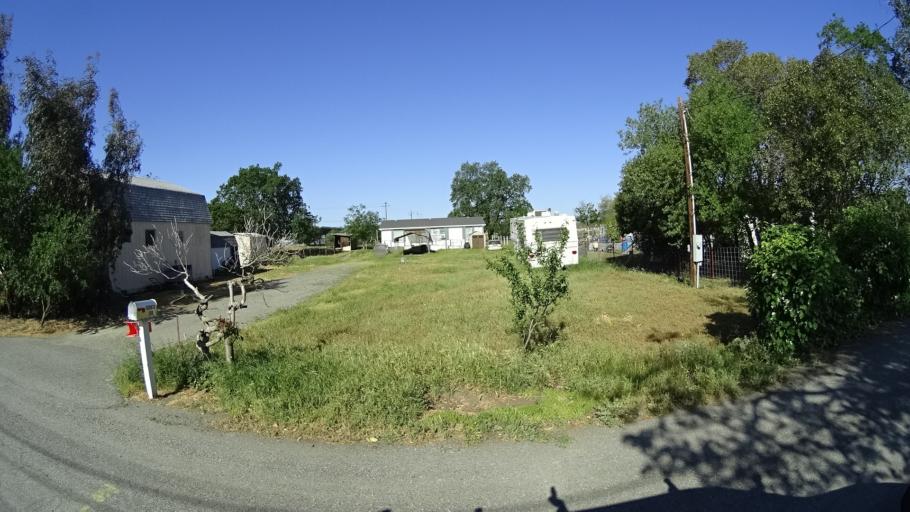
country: US
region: California
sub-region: Glenn County
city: Orland
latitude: 39.7544
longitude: -122.1889
